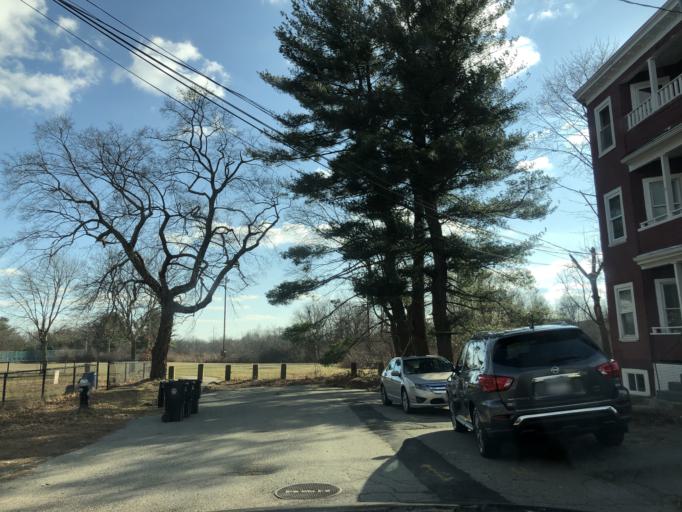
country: US
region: Massachusetts
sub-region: Plymouth County
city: Brockton
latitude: 42.1006
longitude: -71.0142
